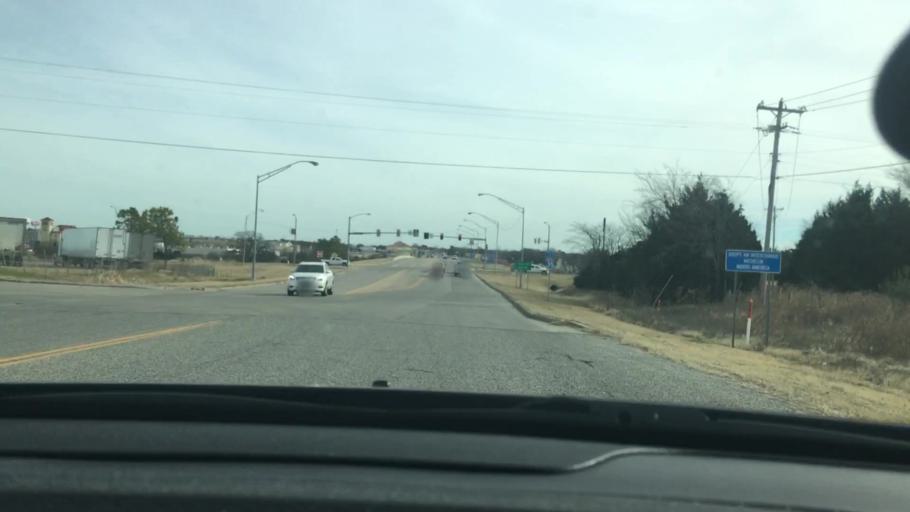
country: US
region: Oklahoma
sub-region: Carter County
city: Ardmore
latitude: 34.1874
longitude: -97.1707
